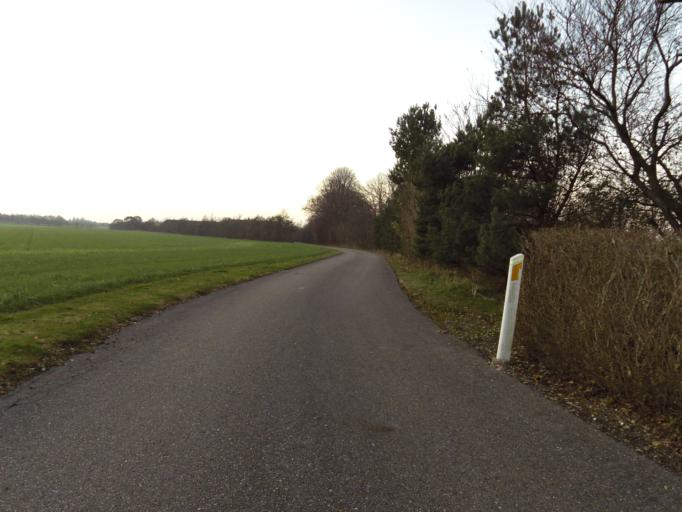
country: DK
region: South Denmark
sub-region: Haderslev Kommune
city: Gram
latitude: 55.2518
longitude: 8.9592
